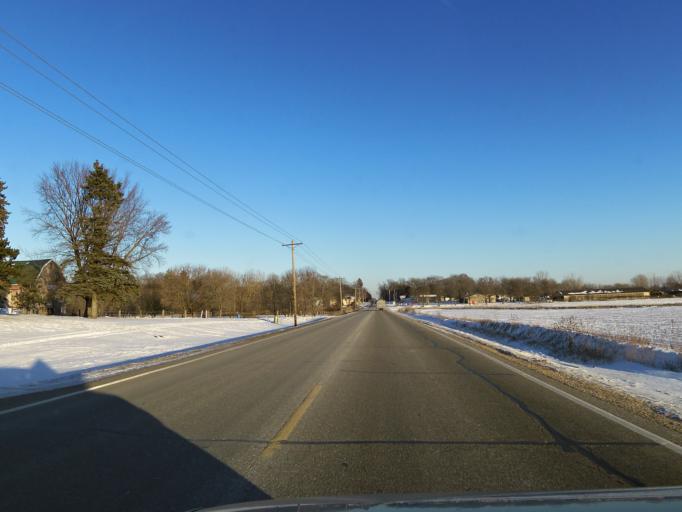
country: US
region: Minnesota
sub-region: Rice County
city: Northfield
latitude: 44.5437
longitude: -93.1603
